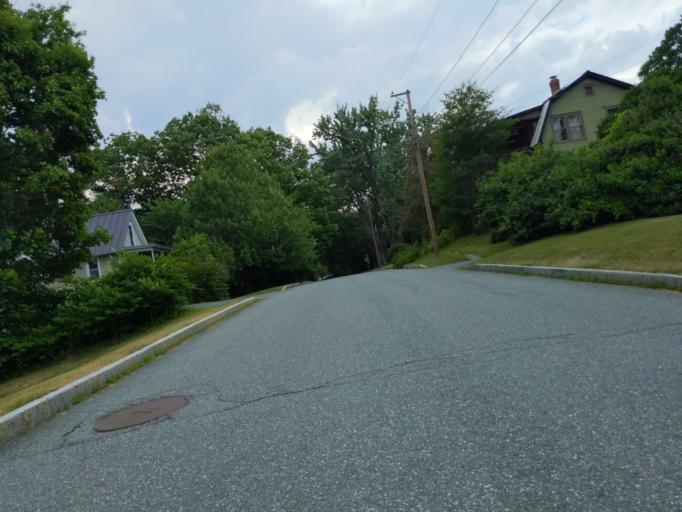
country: US
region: New Hampshire
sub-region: Grafton County
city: Lebanon
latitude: 43.6372
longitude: -72.2448
